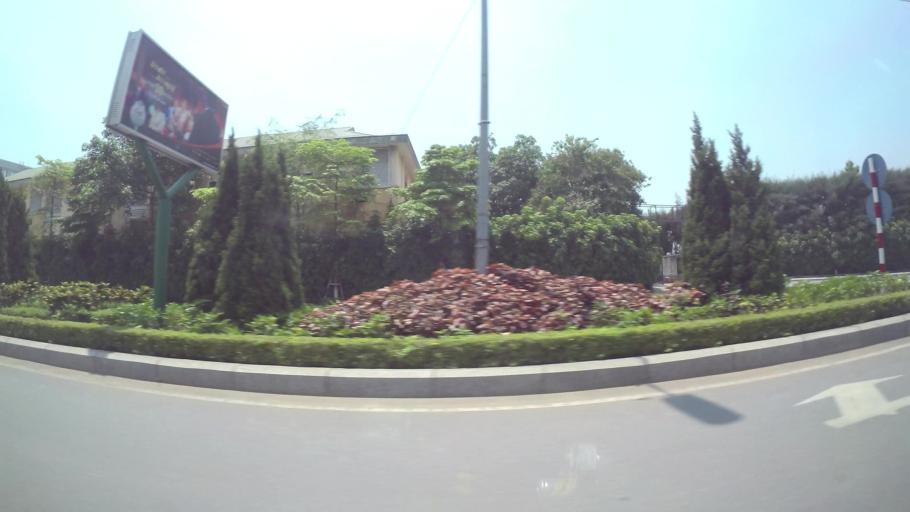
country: VN
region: Ha Noi
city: Trau Quy
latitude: 21.0325
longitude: 105.8991
